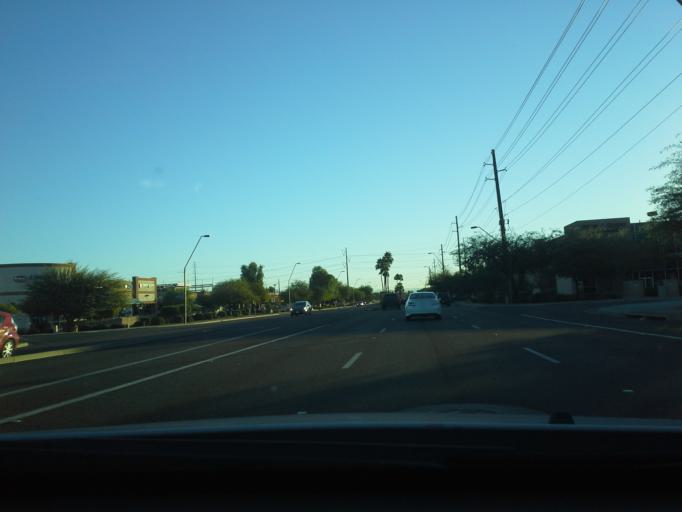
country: US
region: Arizona
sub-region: Maricopa County
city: Guadalupe
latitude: 33.3491
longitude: -111.9509
